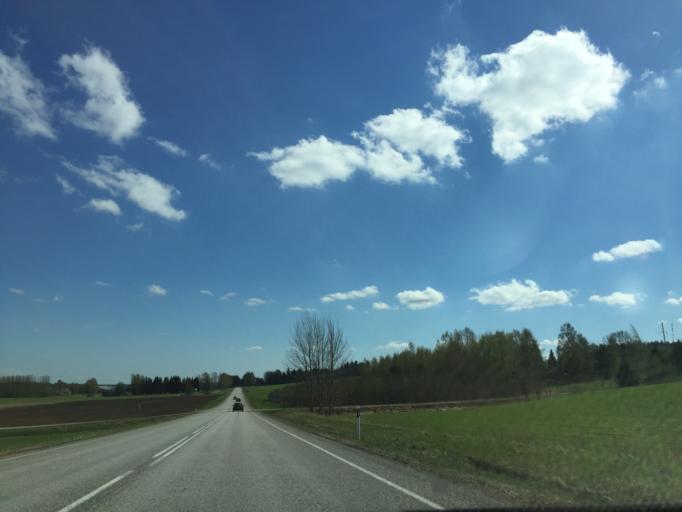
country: EE
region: Valgamaa
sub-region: Valga linn
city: Valga
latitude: 57.8989
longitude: 26.0511
